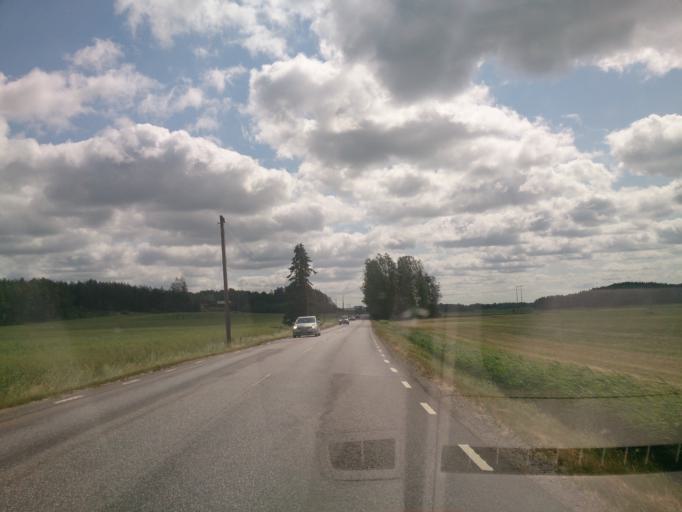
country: SE
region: OEstergoetland
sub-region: Norrkopings Kommun
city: Kimstad
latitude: 58.4828
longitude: 15.9555
